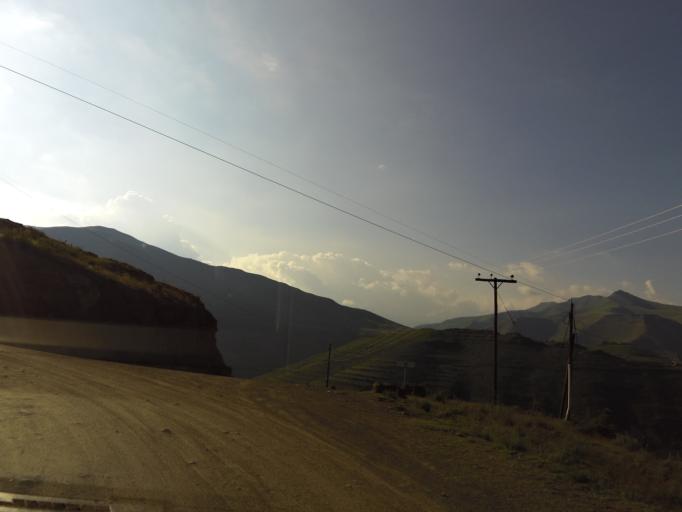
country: LS
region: Butha-Buthe
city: Butha-Buthe
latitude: -29.1041
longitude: 28.5029
